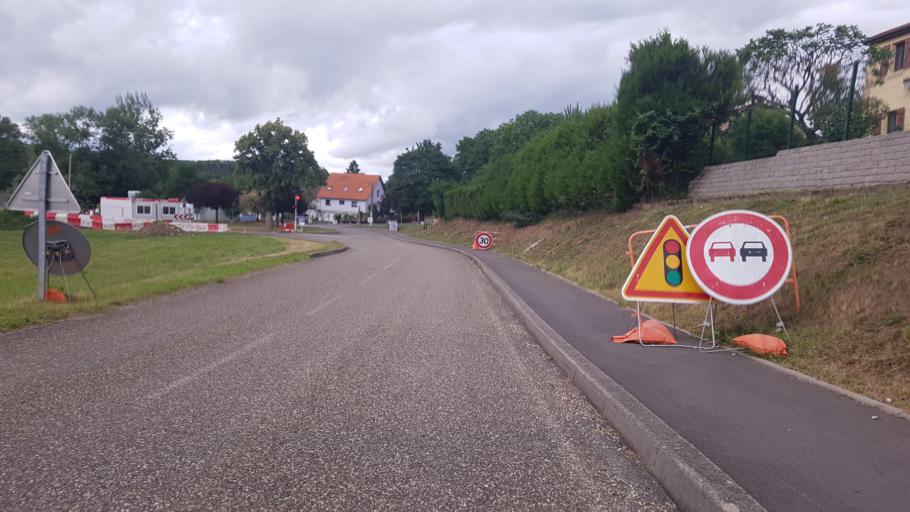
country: FR
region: Lorraine
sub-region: Departement de la Moselle
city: Lorquin
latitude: 48.7005
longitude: 6.9932
